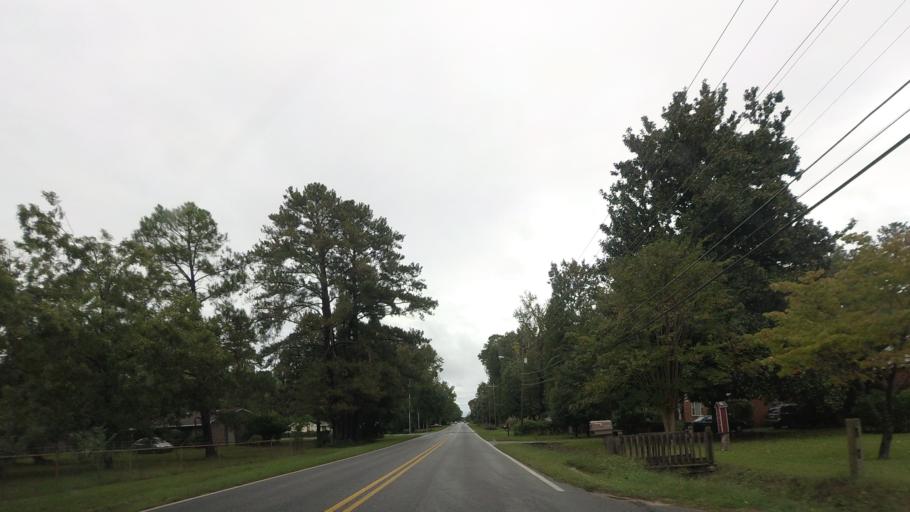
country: US
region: Georgia
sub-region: Houston County
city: Warner Robins
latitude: 32.6101
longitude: -83.6226
